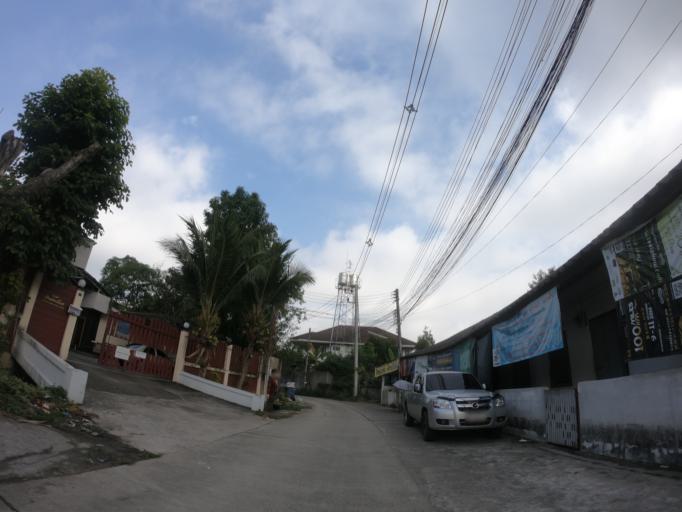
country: TH
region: Chiang Mai
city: Chiang Mai
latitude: 18.7550
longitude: 98.9738
